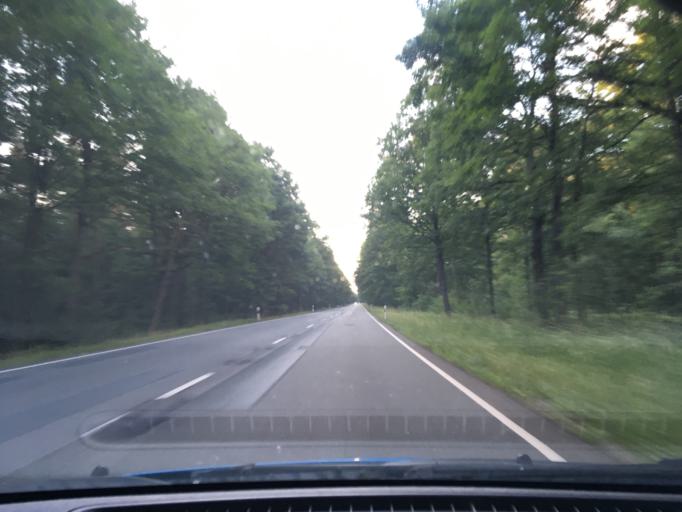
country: DE
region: Lower Saxony
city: Sprakensehl
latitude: 52.8121
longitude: 10.4870
